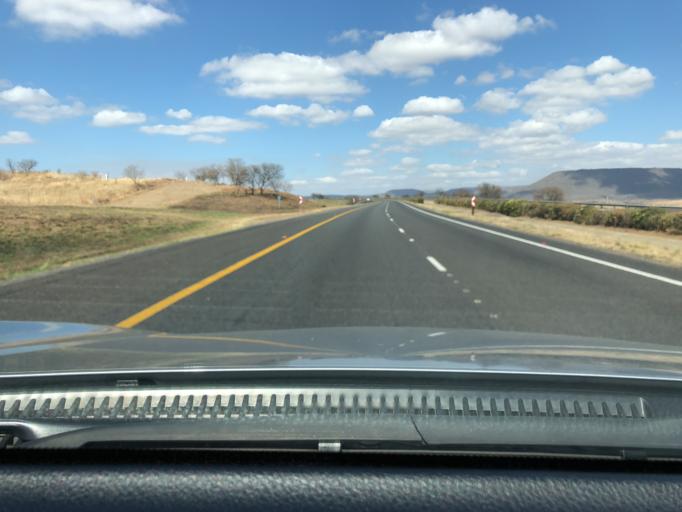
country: ZA
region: KwaZulu-Natal
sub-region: uThukela District Municipality
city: Ladysmith
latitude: -28.6768
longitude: 29.6346
